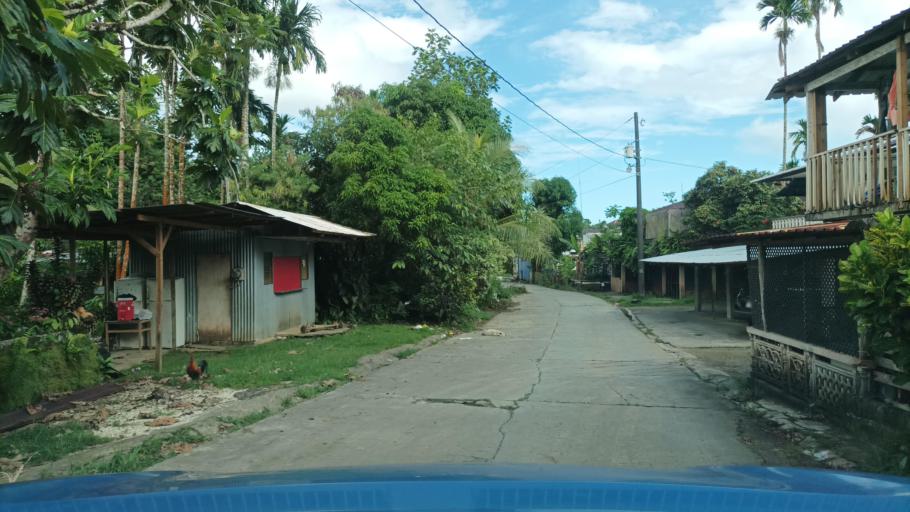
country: FM
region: Pohnpei
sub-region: Kolonia Municipality
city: Kolonia
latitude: 6.9620
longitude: 158.2159
